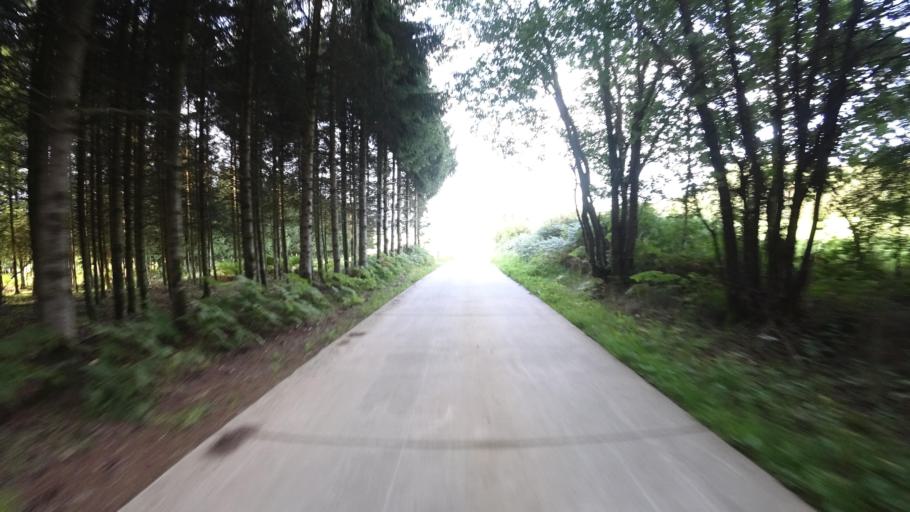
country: BE
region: Wallonia
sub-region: Province du Luxembourg
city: Neufchateau
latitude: 49.8477
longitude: 5.3486
